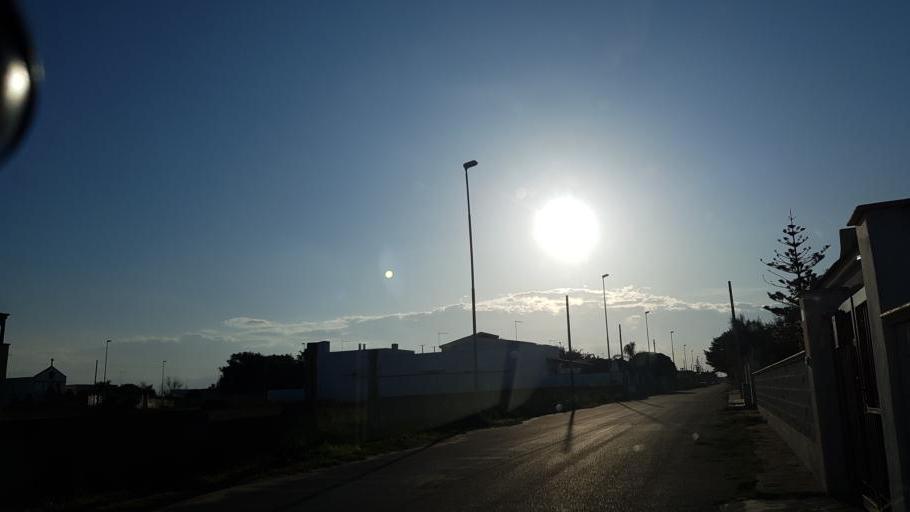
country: IT
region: Apulia
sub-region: Provincia di Brindisi
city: Torchiarolo
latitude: 40.5133
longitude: 18.1000
